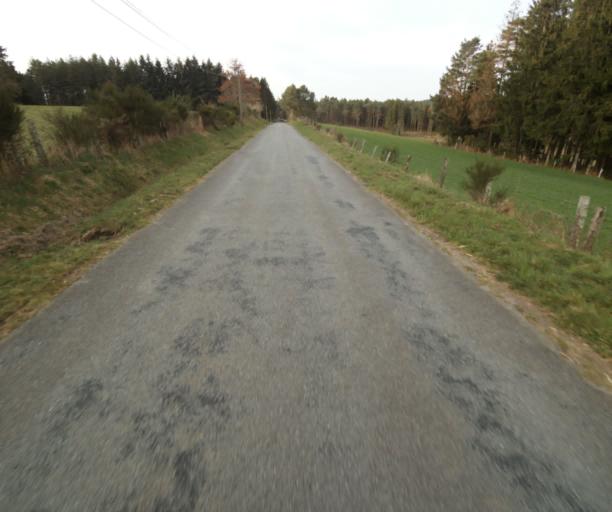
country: FR
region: Limousin
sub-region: Departement de la Correze
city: Treignac
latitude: 45.4645
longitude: 1.8169
